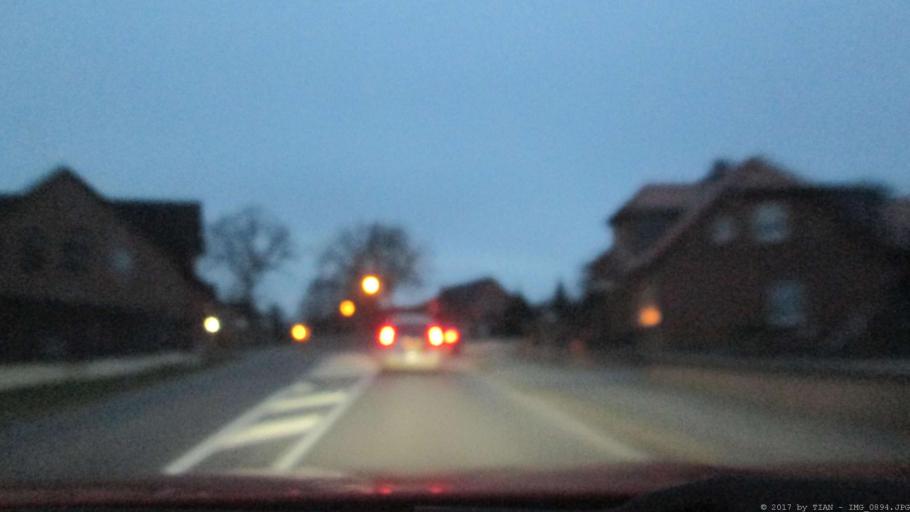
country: DE
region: Lower Saxony
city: Bodenteich
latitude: 52.7976
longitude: 10.7111
